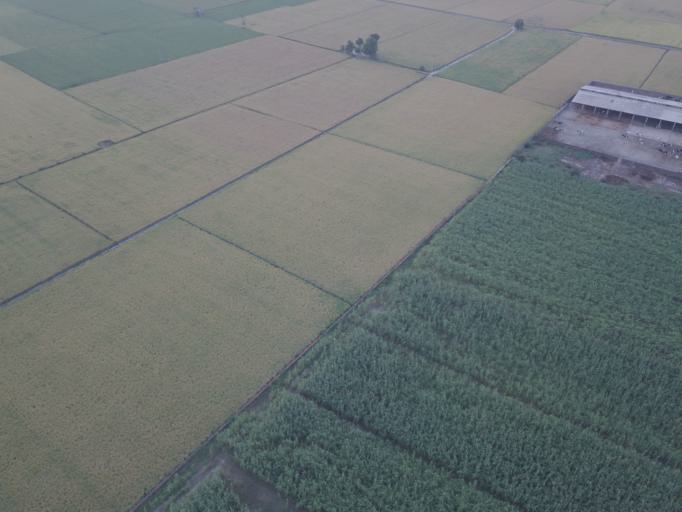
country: IN
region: Punjab
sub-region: Shahid Bhagat Singh Nagar
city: Rahon
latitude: 31.0198
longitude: 76.0936
